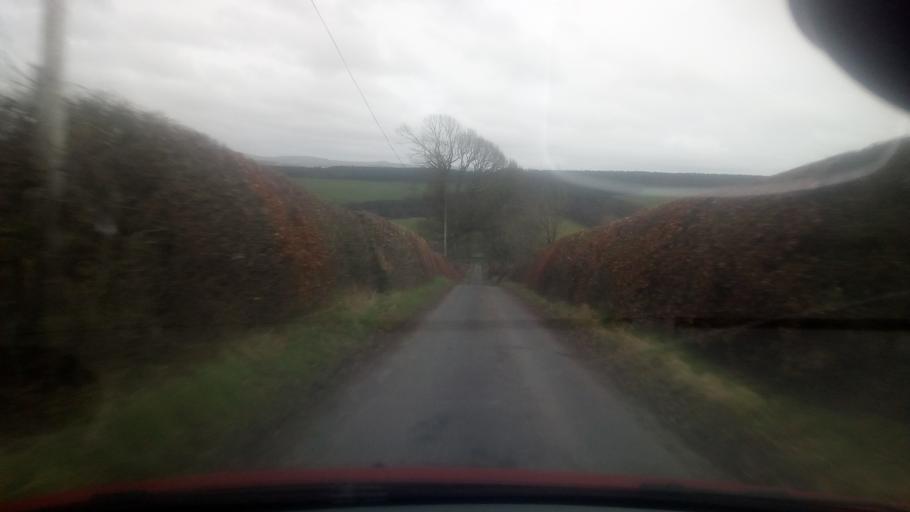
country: GB
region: Scotland
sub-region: The Scottish Borders
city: Jedburgh
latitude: 55.4614
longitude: -2.5161
